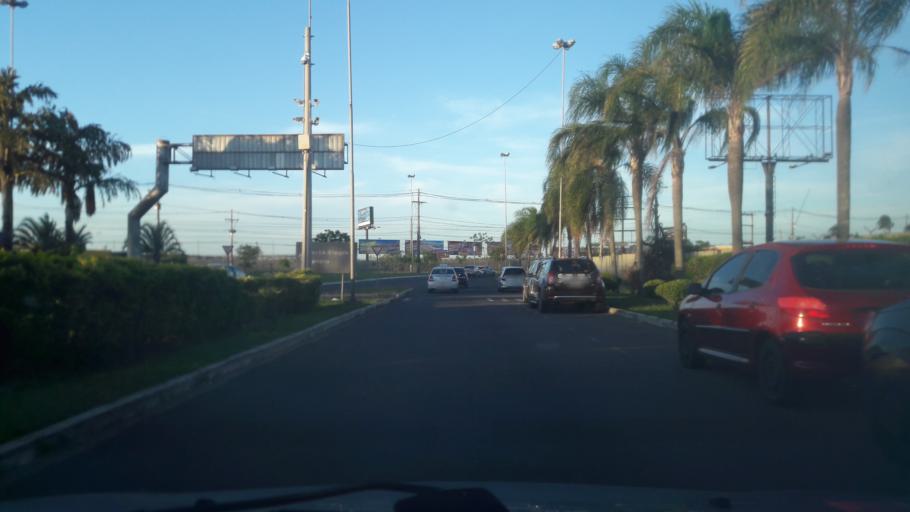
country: BR
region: Rio Grande do Sul
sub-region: Porto Alegre
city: Porto Alegre
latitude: -29.9892
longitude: -51.1737
